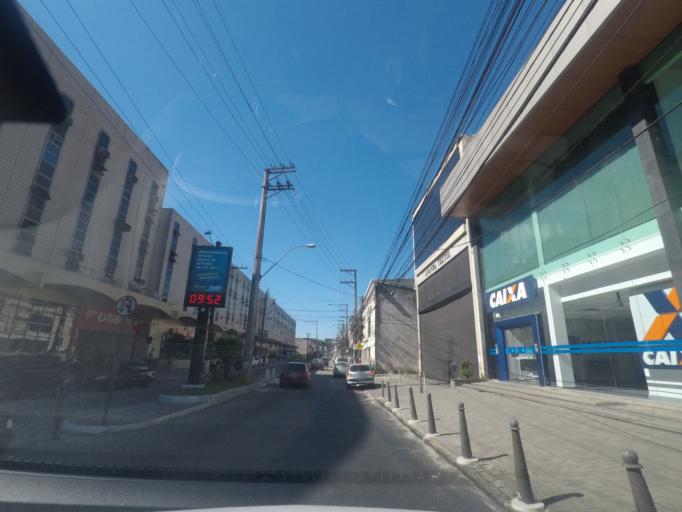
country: BR
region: Rio de Janeiro
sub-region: Petropolis
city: Petropolis
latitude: -22.5235
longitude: -43.1709
